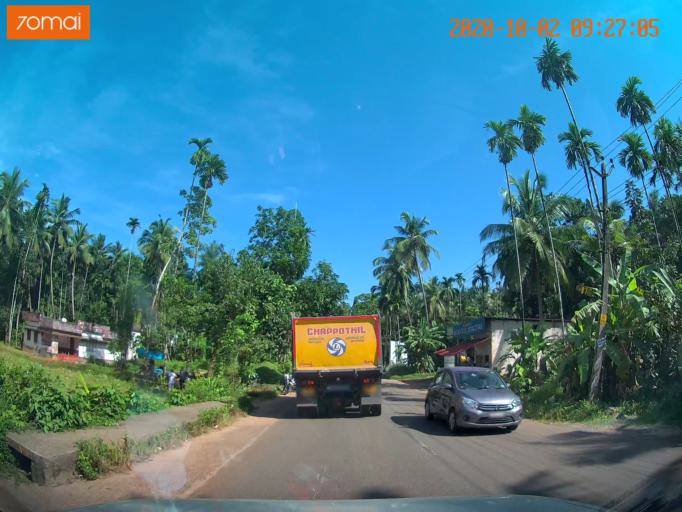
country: IN
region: Kerala
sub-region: Kozhikode
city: Naduvannur
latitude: 11.5965
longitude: 75.7651
